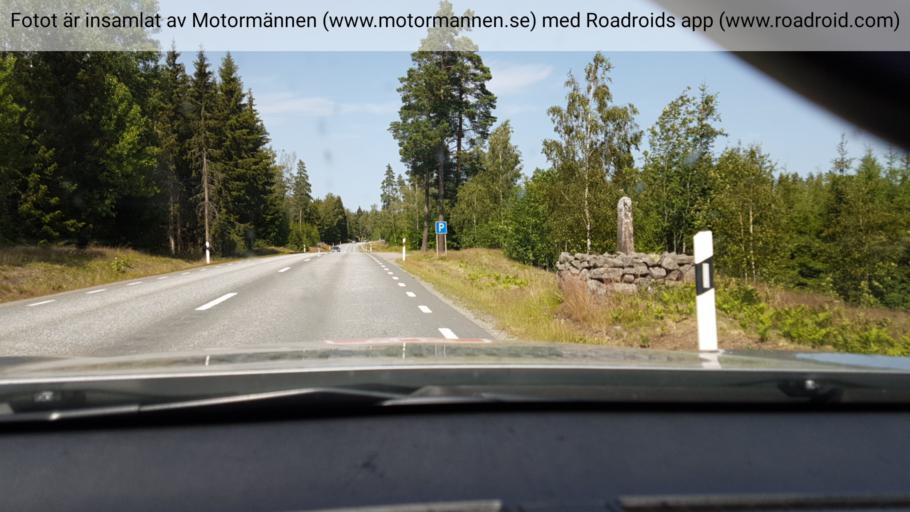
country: SE
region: Joenkoeping
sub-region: Nassjo Kommun
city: Bodafors
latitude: 57.5340
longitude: 14.7870
